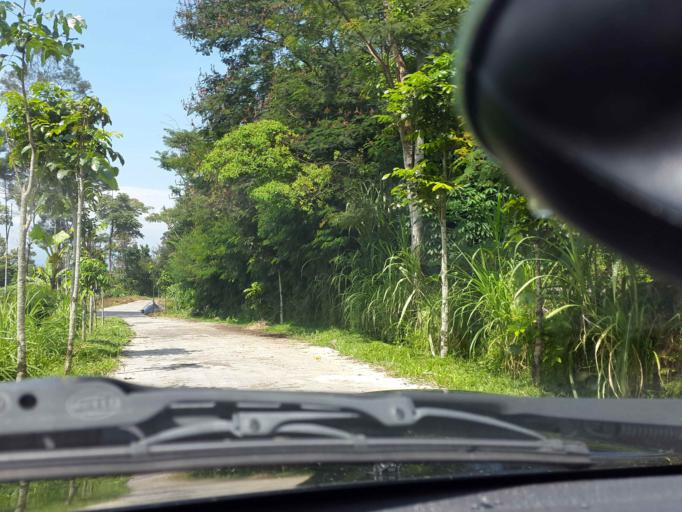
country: ID
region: Central Java
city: Wonosobo
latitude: -7.3643
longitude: 109.9817
